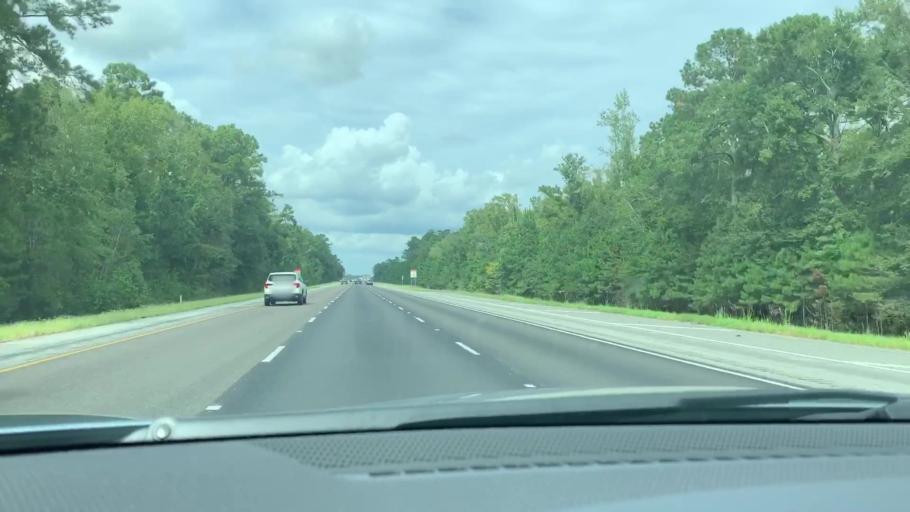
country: US
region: Georgia
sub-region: Liberty County
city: Midway
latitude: 31.7192
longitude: -81.3891
